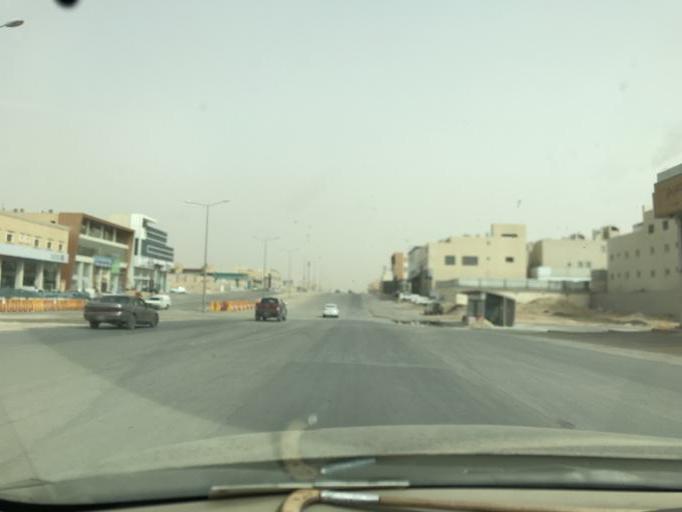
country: SA
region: Ar Riyad
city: Riyadh
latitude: 24.8153
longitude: 46.5982
